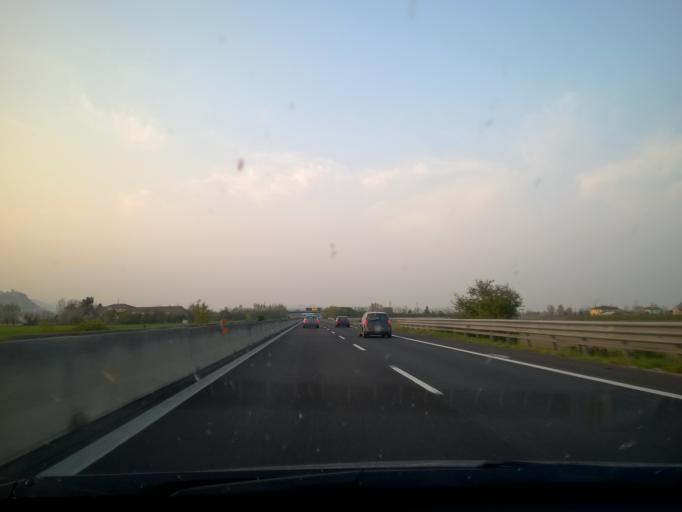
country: IT
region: Veneto
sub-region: Provincia di Padova
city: Pozzonovo
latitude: 45.2179
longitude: 11.7746
